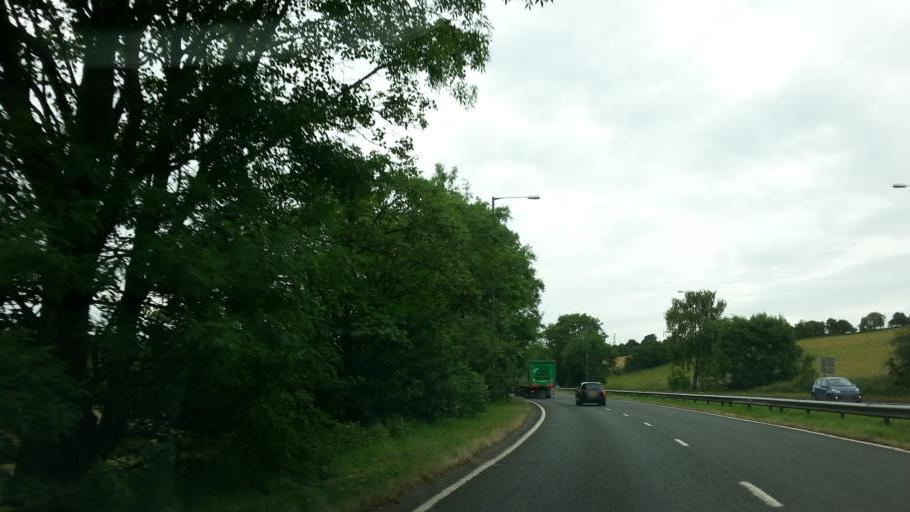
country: GB
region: England
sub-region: Worcestershire
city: Barnt Green
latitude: 52.3848
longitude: -2.0308
